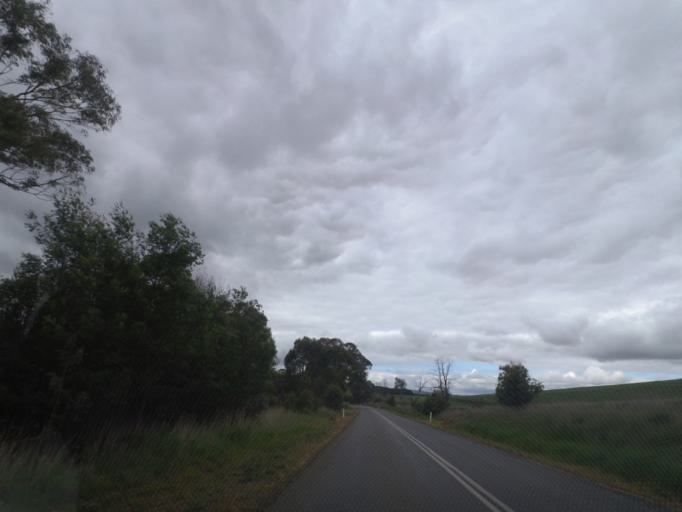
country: AU
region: Victoria
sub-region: Hume
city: Sunbury
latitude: -37.3969
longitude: 144.8521
